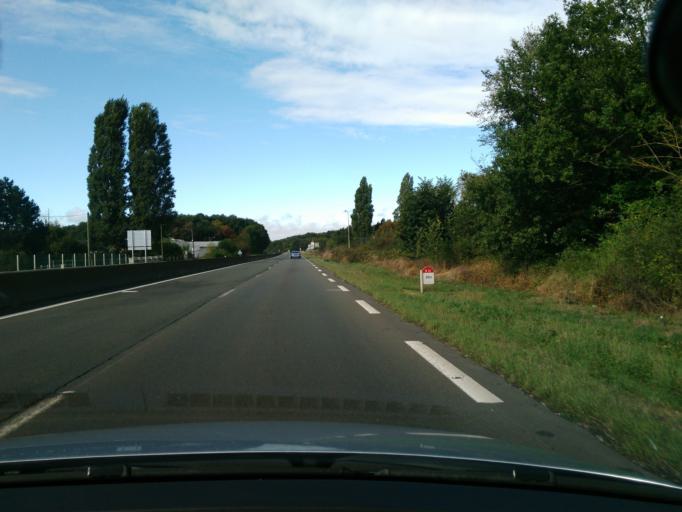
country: FR
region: Centre
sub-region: Departement d'Eure-et-Loir
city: Dreux
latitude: 48.7425
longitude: 1.3322
